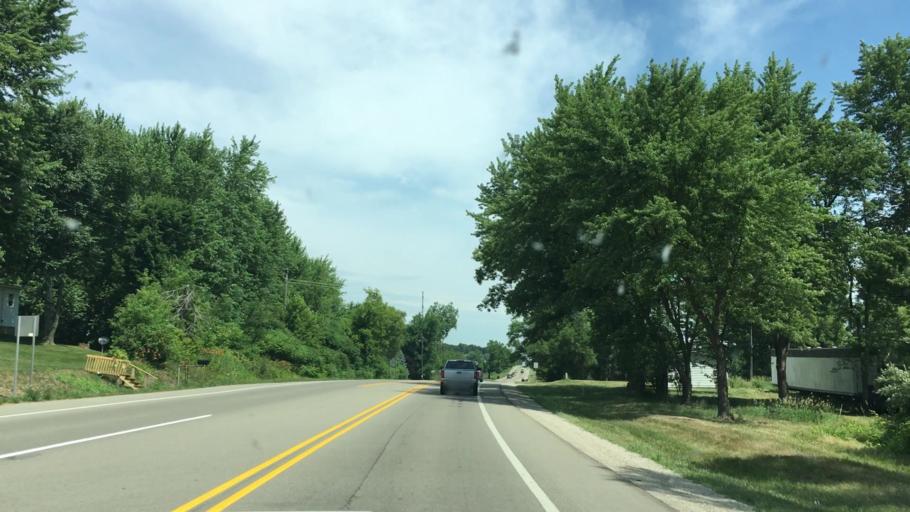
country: US
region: Michigan
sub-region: Lapeer County
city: Imlay City
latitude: 43.0662
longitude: -83.0745
